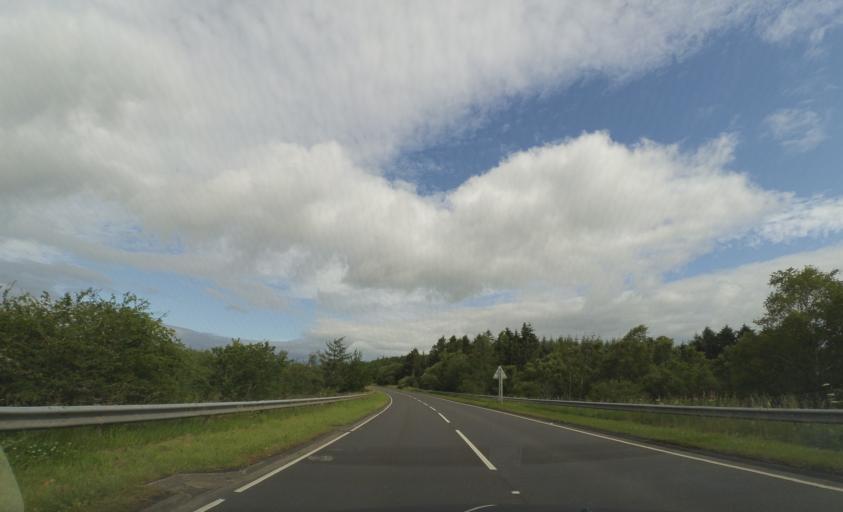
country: GB
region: Scotland
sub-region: The Scottish Borders
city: Selkirk
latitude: 55.5337
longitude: -2.8272
